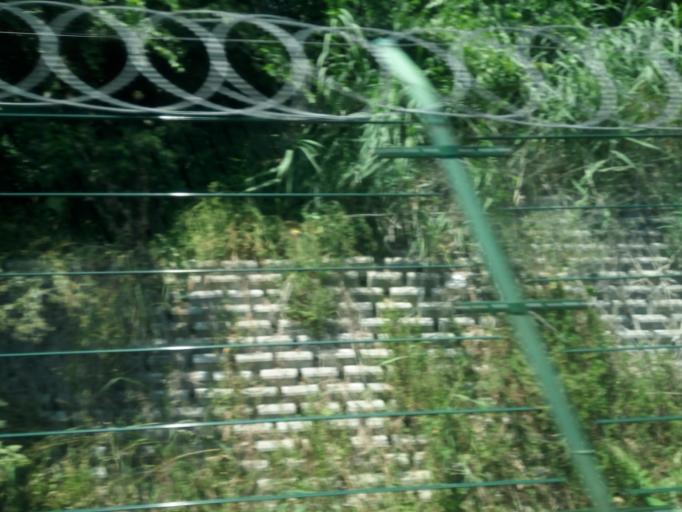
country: TR
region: Istanbul
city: guengoeren merter
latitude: 40.9995
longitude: 28.8824
